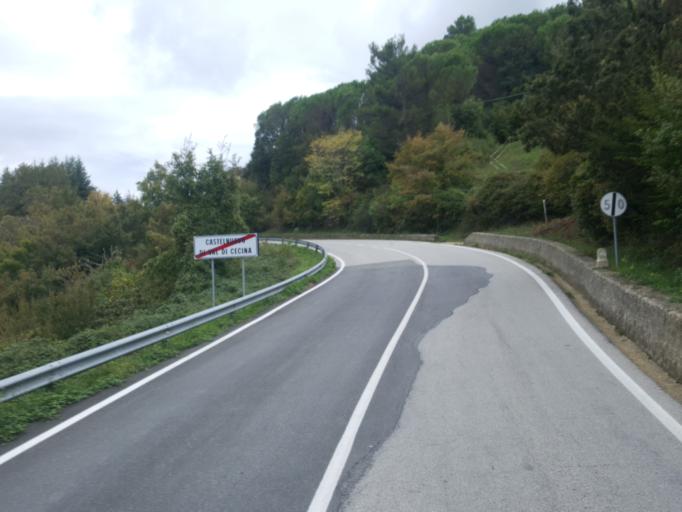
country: IT
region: Tuscany
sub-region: Province of Pisa
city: Castelnuovo di Val di Cecina
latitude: 43.2050
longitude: 10.9062
